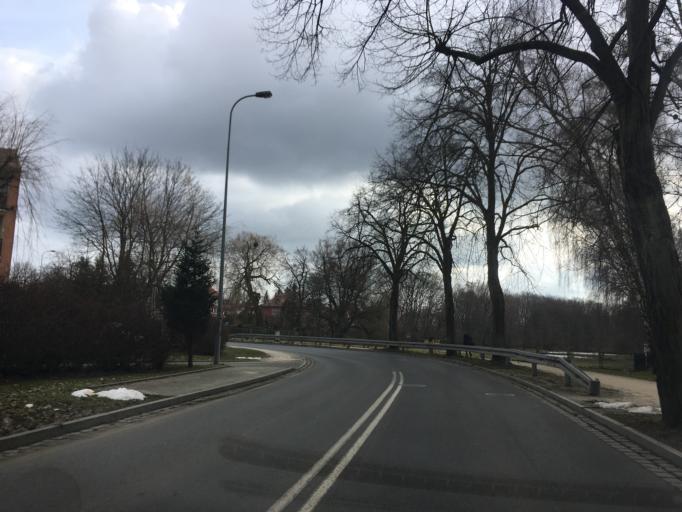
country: PL
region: Pomeranian Voivodeship
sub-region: Slupsk
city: Slupsk
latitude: 54.4606
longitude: 17.0407
